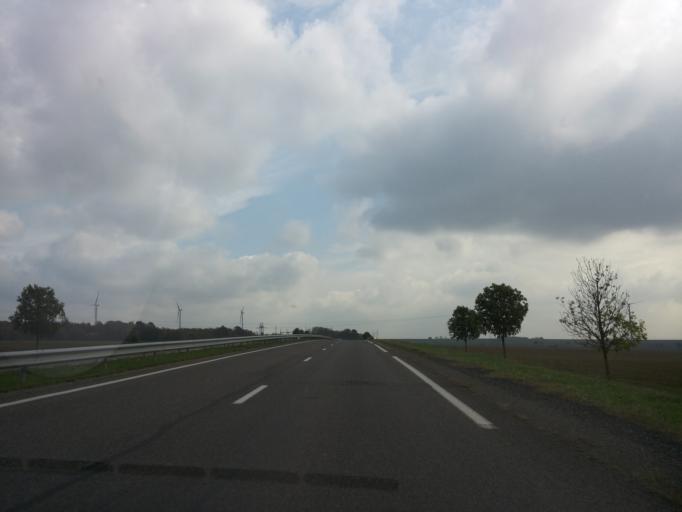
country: FR
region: Lorraine
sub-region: Departement de la Moselle
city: Chateau-Salins
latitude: 48.8532
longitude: 6.4484
